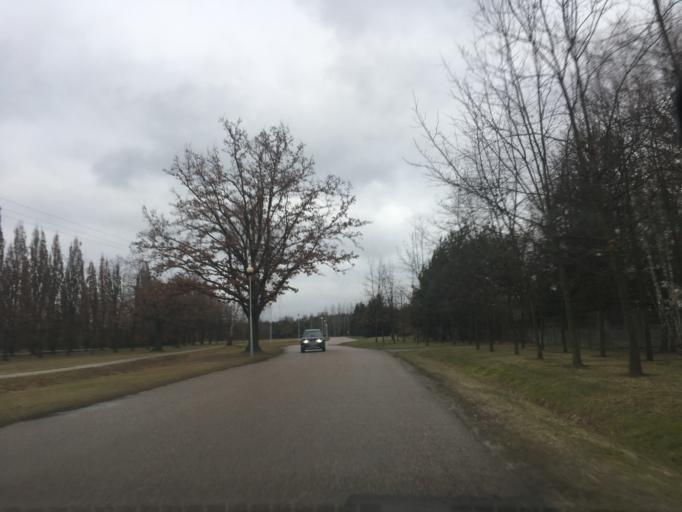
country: PL
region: Masovian Voivodeship
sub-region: Powiat piaseczynski
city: Lesznowola
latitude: 52.0583
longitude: 20.9062
